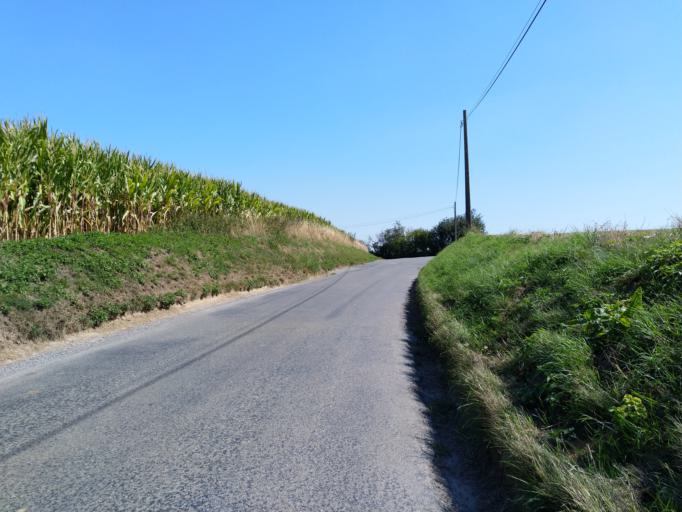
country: BE
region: Wallonia
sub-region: Province du Hainaut
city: Roeulx
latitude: 50.5005
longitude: 4.0918
